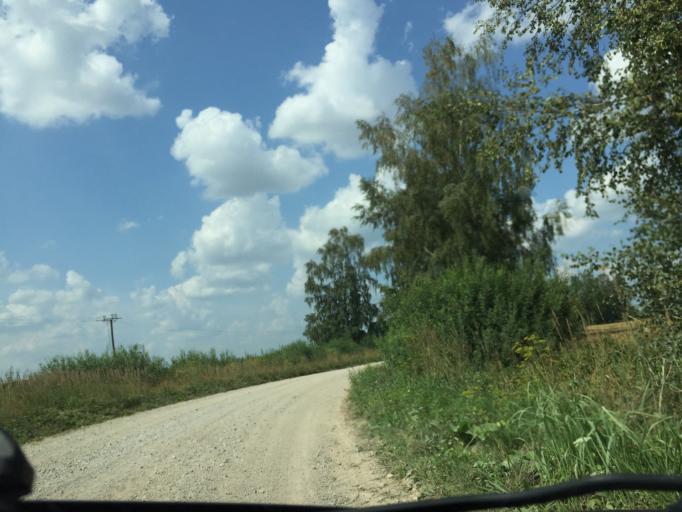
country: LT
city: Zagare
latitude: 56.3893
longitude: 23.2571
